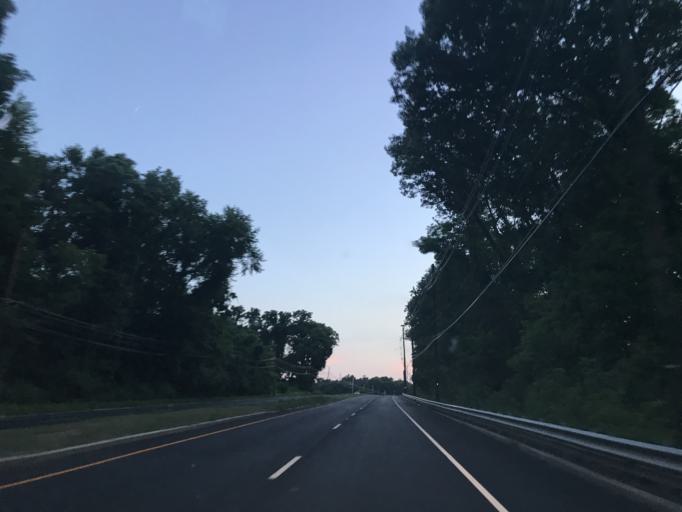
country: US
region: New Jersey
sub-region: Burlington County
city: Bordentown
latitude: 40.1239
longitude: -74.7422
